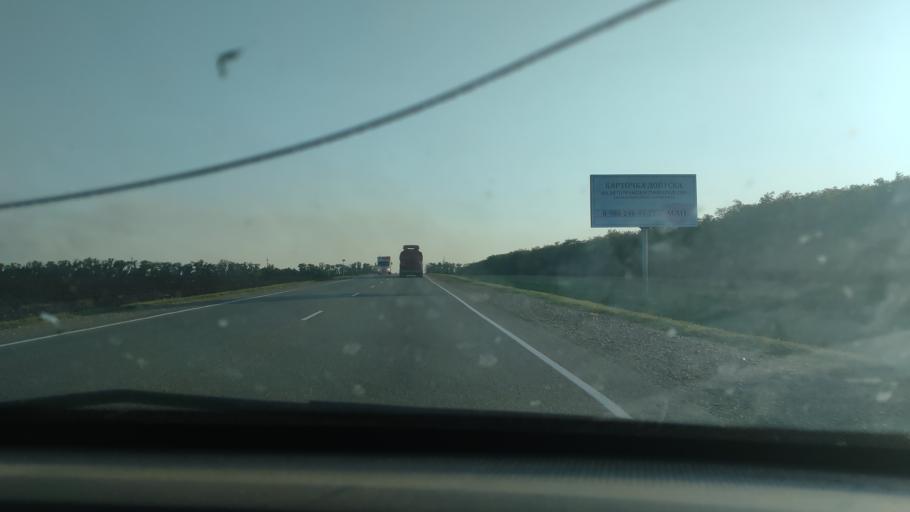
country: RU
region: Krasnodarskiy
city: Kanevskaya
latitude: 46.0372
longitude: 38.9822
